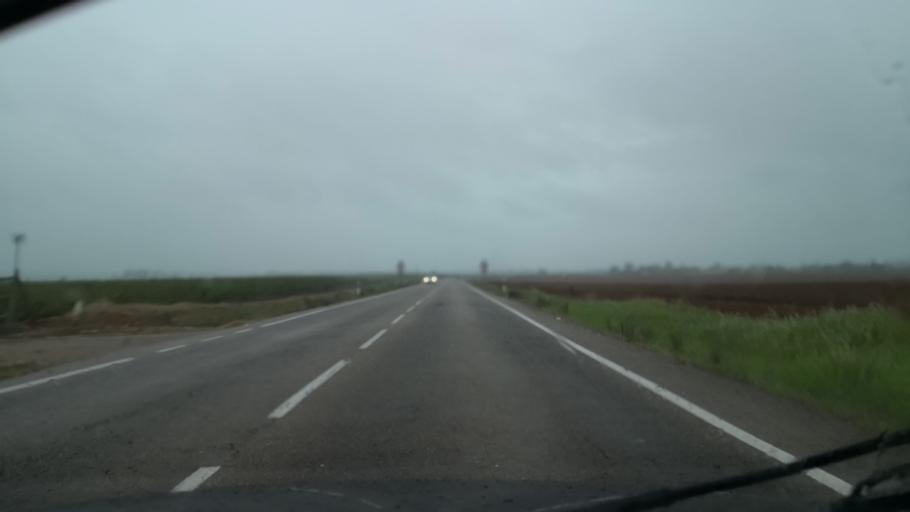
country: ES
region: Extremadura
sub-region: Provincia de Badajoz
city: Badajoz
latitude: 38.9357
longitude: -6.9235
